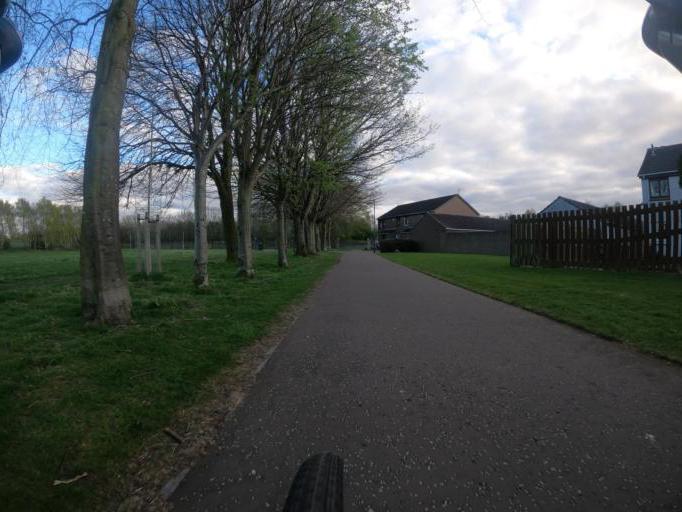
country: GB
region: Scotland
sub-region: Edinburgh
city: Currie
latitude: 55.9390
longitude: -3.3068
